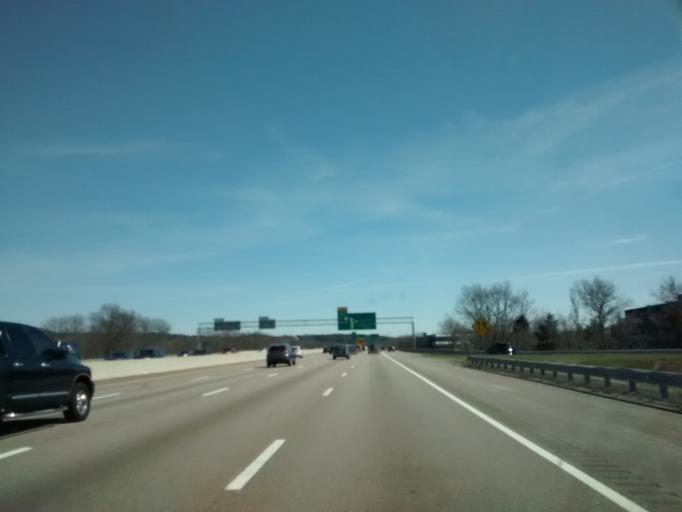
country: US
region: Massachusetts
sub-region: Norfolk County
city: Dedham
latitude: 42.2137
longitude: -71.1515
